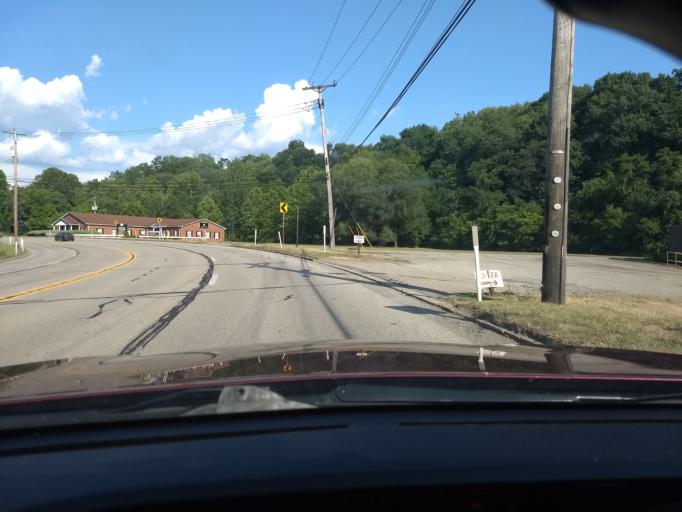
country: US
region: Pennsylvania
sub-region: Allegheny County
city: Versailles
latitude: 40.3213
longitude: -79.8295
